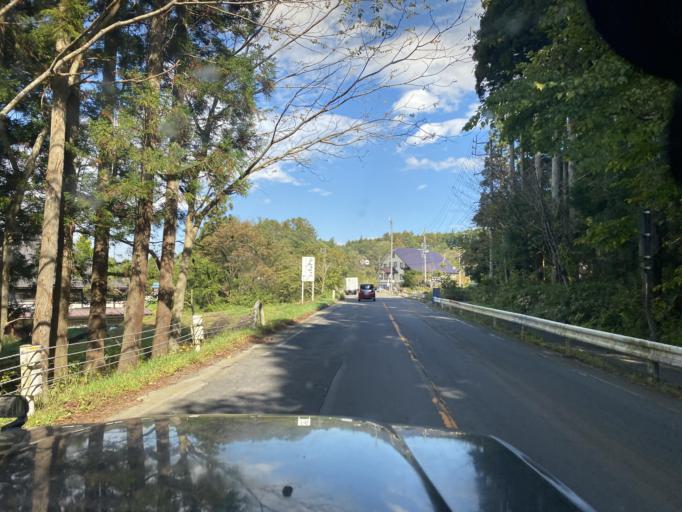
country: JP
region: Nagano
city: Omachi
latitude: 36.5941
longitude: 137.8452
